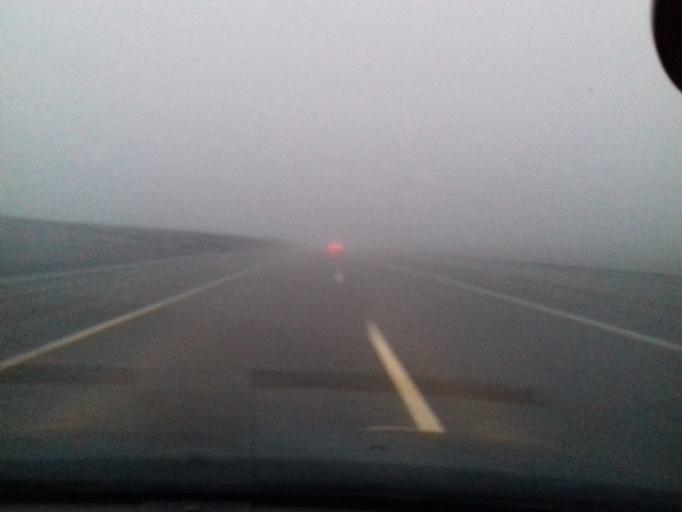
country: HU
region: Hajdu-Bihar
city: Hajdunanas
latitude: 47.8964
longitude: 21.4737
